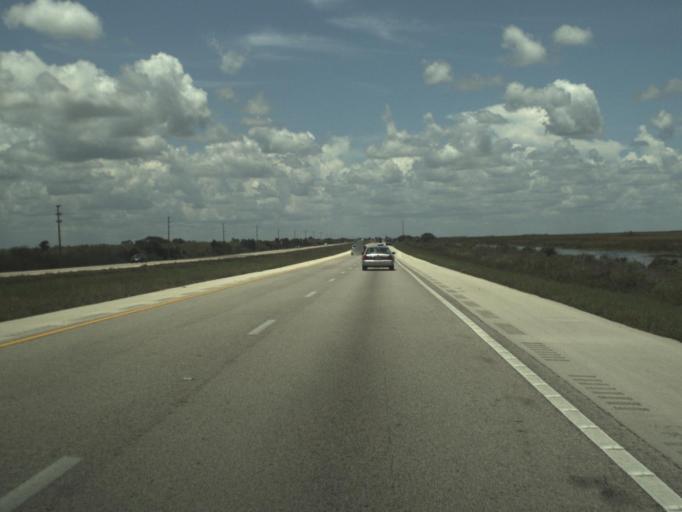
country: US
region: Florida
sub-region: Broward County
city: Weston
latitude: 26.1466
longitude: -80.6673
